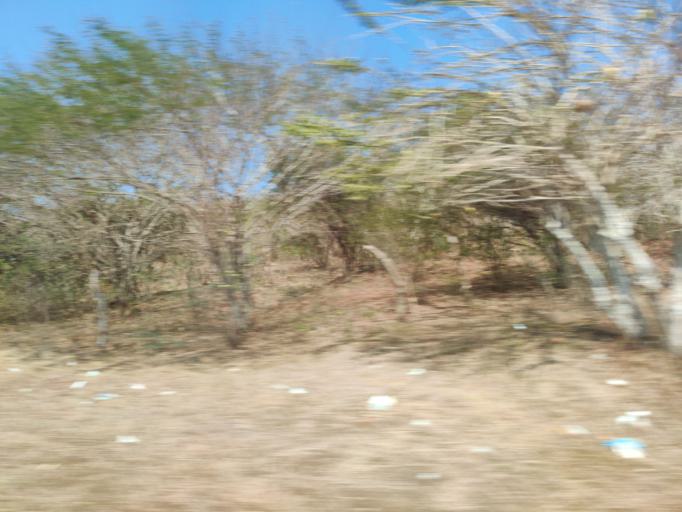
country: CO
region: Bolivar
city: Santa Catalina
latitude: 10.7426
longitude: -75.2540
